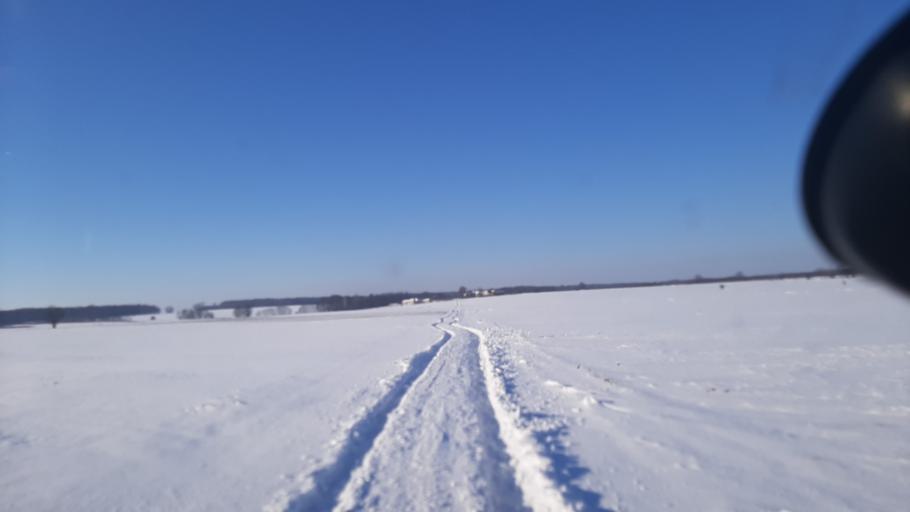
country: PL
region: Lublin Voivodeship
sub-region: Powiat lubelski
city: Jastkow
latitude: 51.3797
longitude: 22.4310
